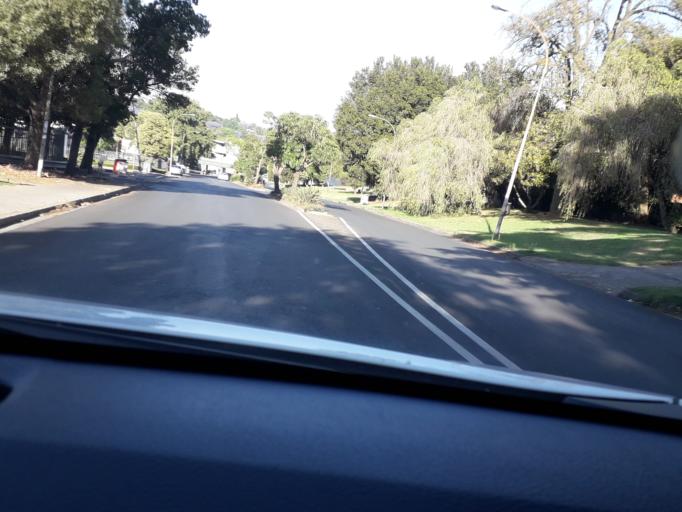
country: ZA
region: Gauteng
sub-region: City of Johannesburg Metropolitan Municipality
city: Johannesburg
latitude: -26.1459
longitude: 28.0795
